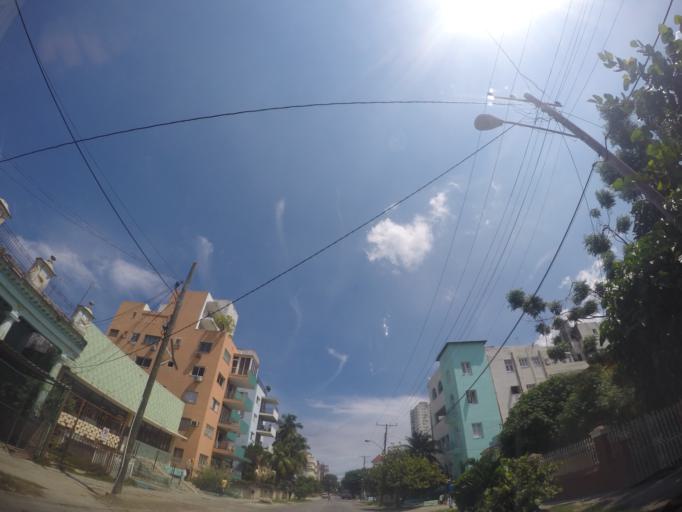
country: CU
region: La Habana
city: Havana
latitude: 23.1397
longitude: -82.3981
